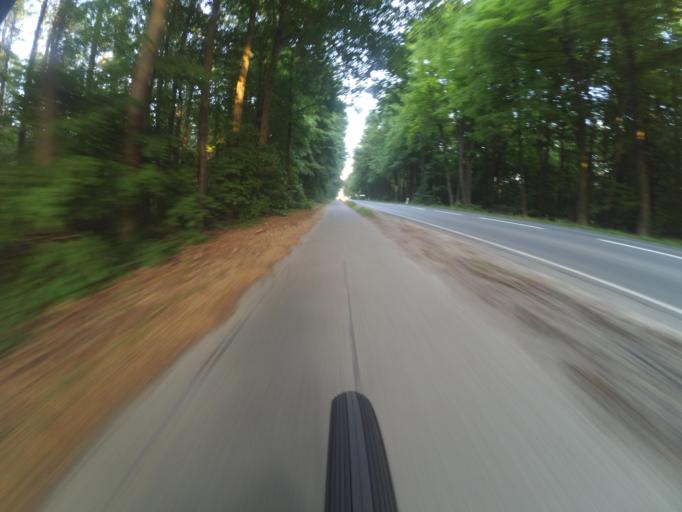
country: DE
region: North Rhine-Westphalia
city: Ibbenburen
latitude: 52.3050
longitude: 7.6866
